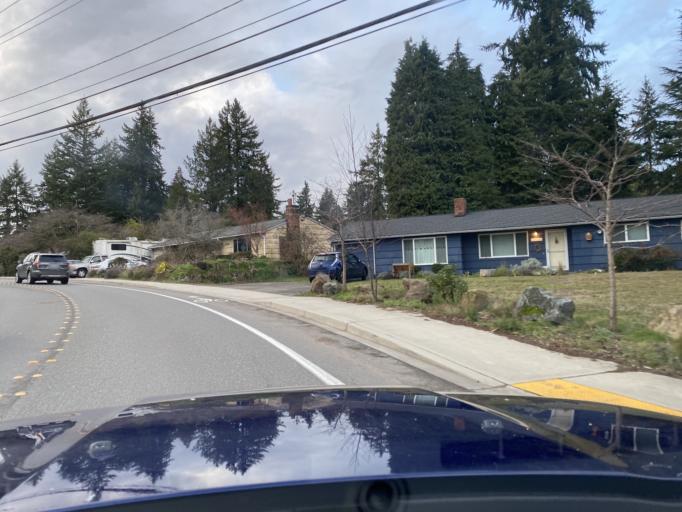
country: US
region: Washington
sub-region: King County
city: Eastgate
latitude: 47.5713
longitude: -122.1377
